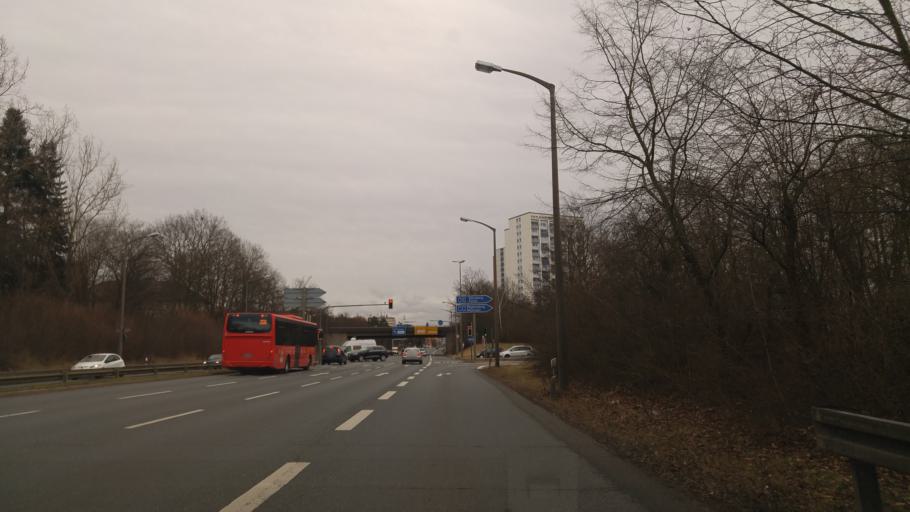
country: DE
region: Bavaria
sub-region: Regierungsbezirk Mittelfranken
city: Erlangen
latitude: 49.5825
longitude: 10.9859
